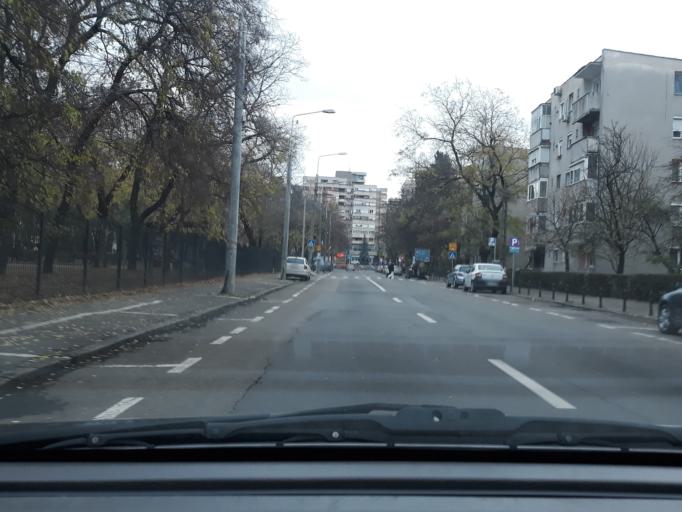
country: RO
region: Bihor
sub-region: Comuna Biharea
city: Oradea
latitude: 47.0521
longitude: 21.9354
